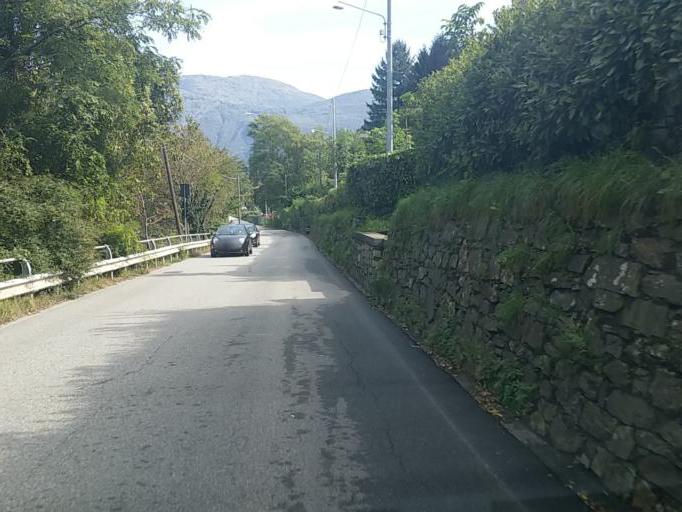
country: IT
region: Piedmont
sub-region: Provincia Verbano-Cusio-Ossola
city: Cannobio
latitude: 46.0571
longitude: 8.6834
